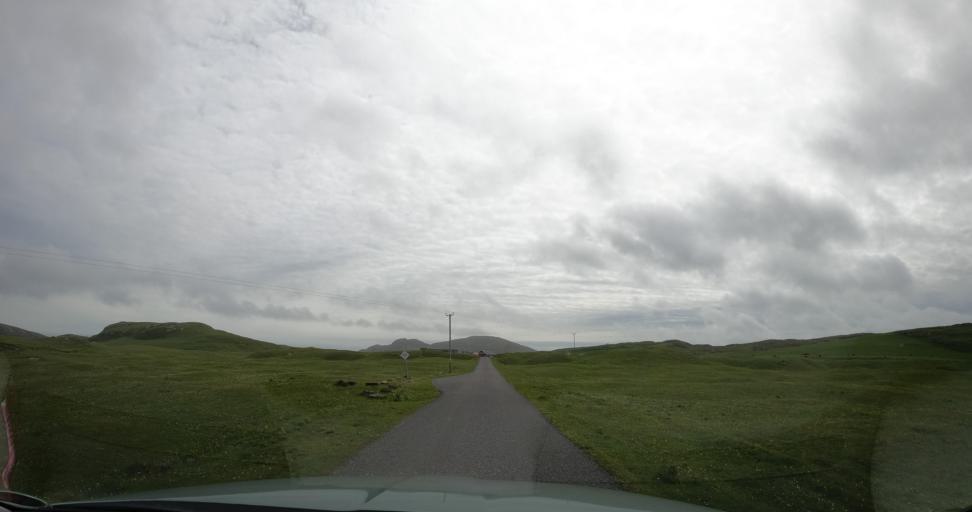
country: GB
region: Scotland
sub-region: Eilean Siar
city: Barra
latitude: 56.9229
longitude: -7.5386
